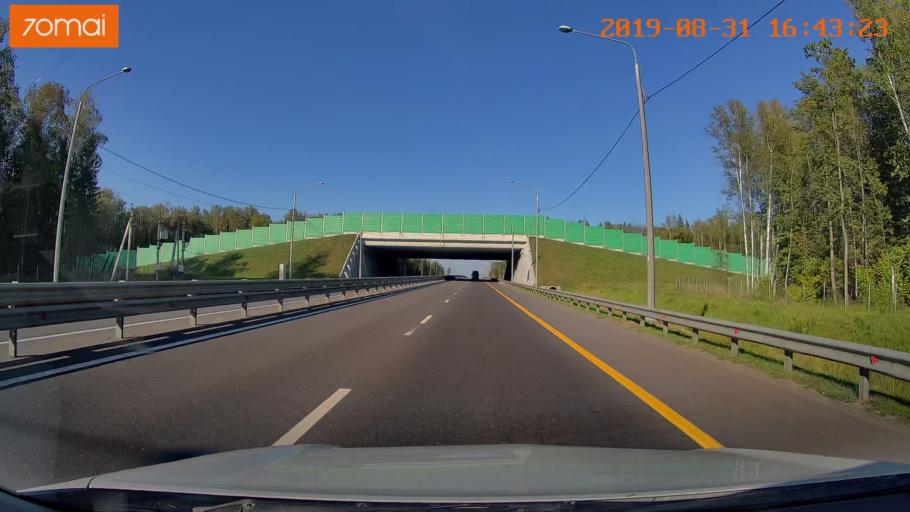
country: RU
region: Kaluga
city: Mstikhino
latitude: 54.6085
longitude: 36.1035
